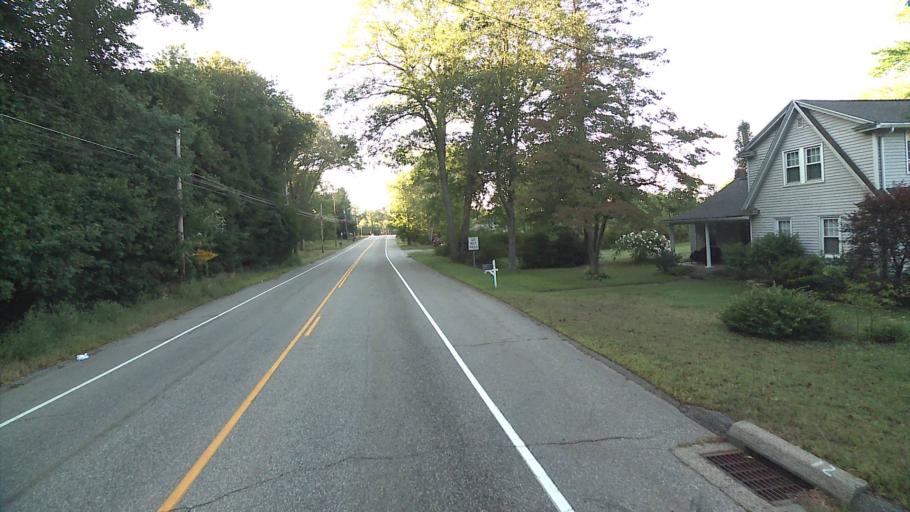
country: US
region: Connecticut
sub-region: Tolland County
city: Mansfield City
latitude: 41.7581
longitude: -72.2650
